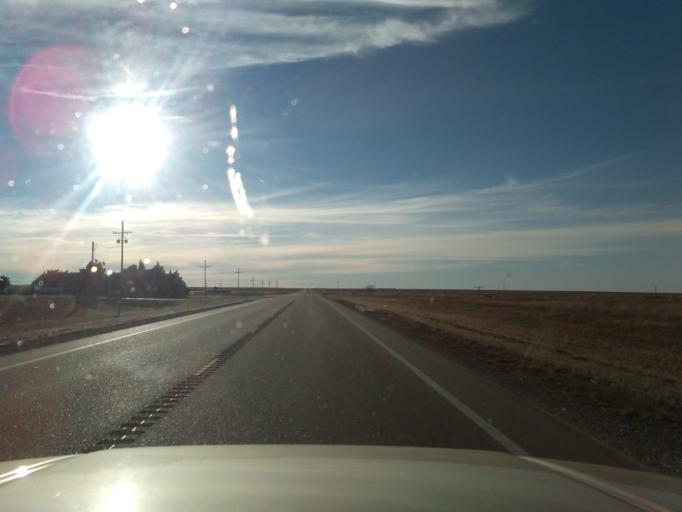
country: US
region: Kansas
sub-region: Sheridan County
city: Hoxie
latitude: 39.5368
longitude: -100.5849
